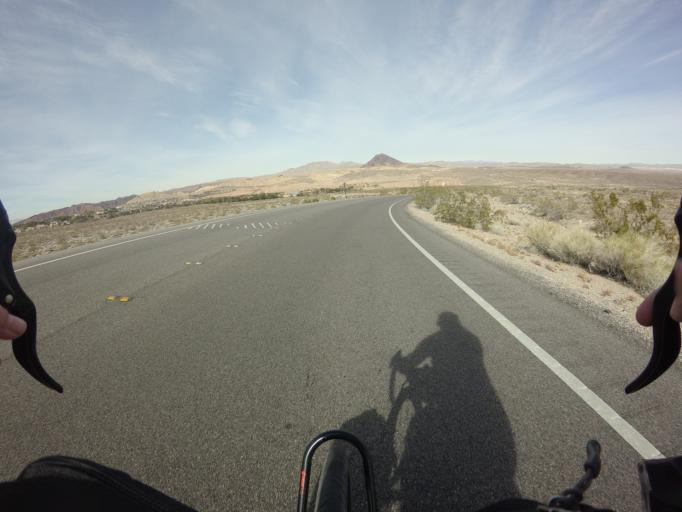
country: US
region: Nevada
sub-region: Clark County
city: Henderson
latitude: 36.1102
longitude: -114.9005
